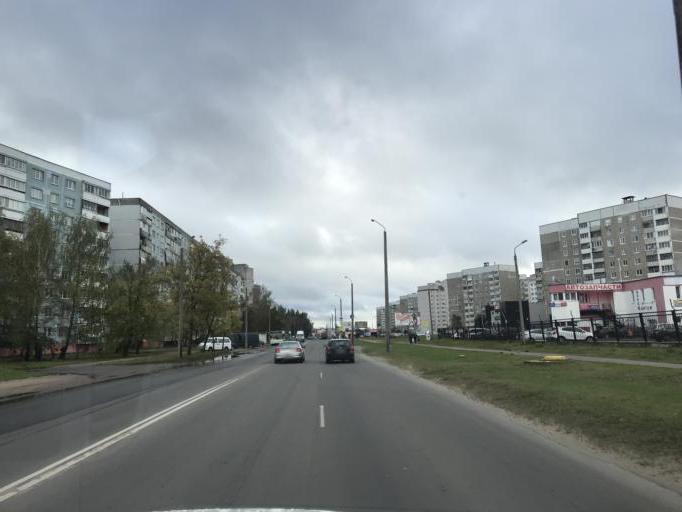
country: BY
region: Mogilev
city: Mahilyow
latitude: 53.8786
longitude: 30.3687
